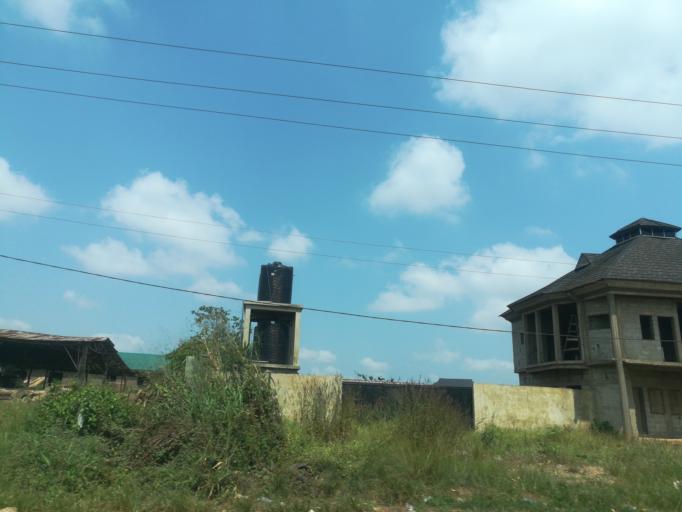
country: NG
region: Ogun
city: Abeokuta
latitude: 7.1398
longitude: 3.4060
